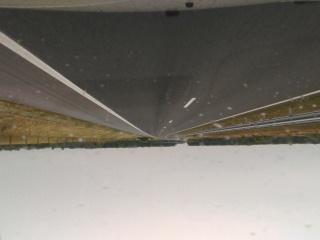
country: BG
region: Stara Zagora
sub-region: Obshtina Stara Zagora
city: Stara Zagora
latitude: 42.3496
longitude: 25.7297
